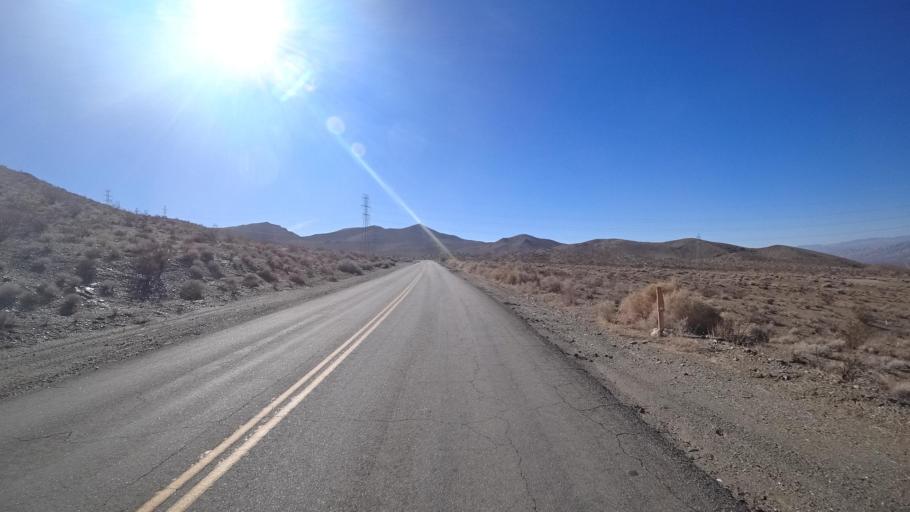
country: US
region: California
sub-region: Kern County
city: Ridgecrest
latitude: 35.3775
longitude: -117.6538
